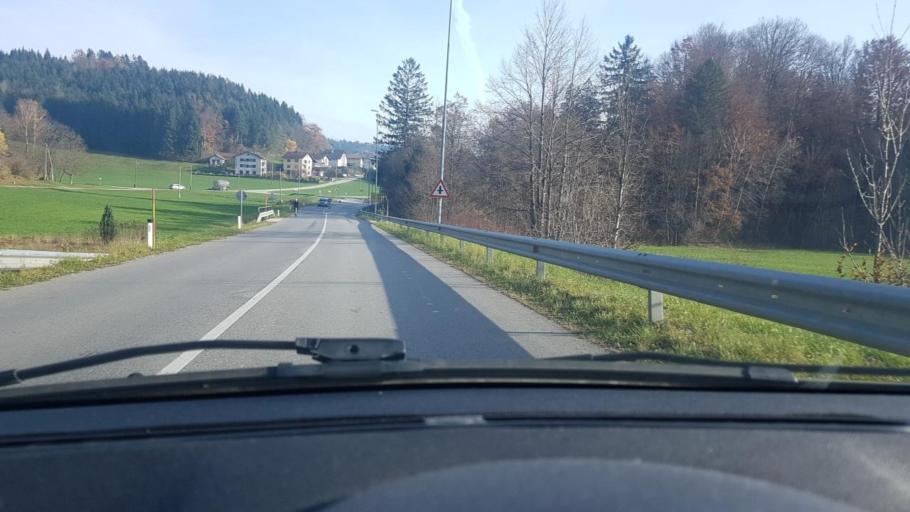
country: SI
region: Kranj
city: Golnik
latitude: 46.3221
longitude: 14.3396
